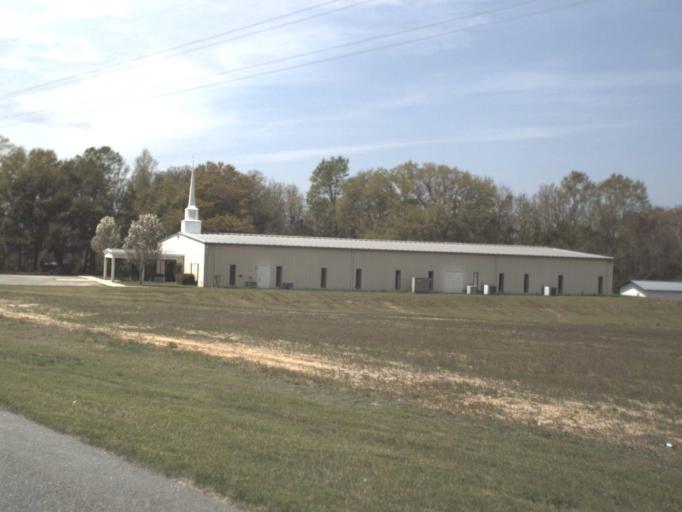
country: US
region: Florida
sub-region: Jackson County
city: Graceville
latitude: 30.9733
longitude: -85.5016
